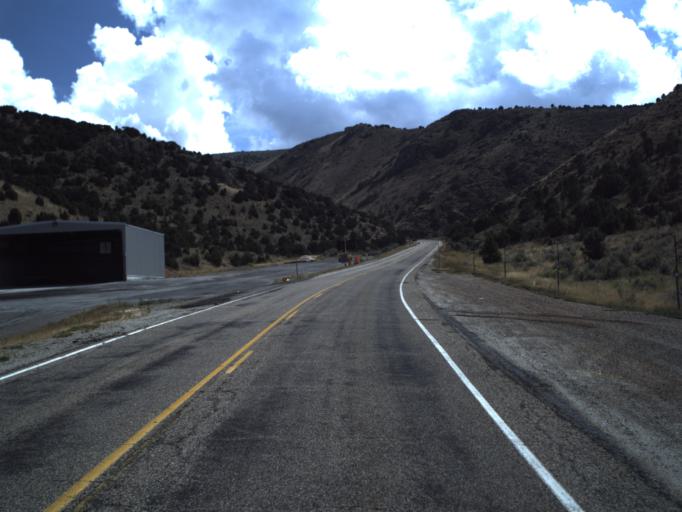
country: US
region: Utah
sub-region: Rich County
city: Randolph
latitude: 41.8275
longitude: -111.3131
